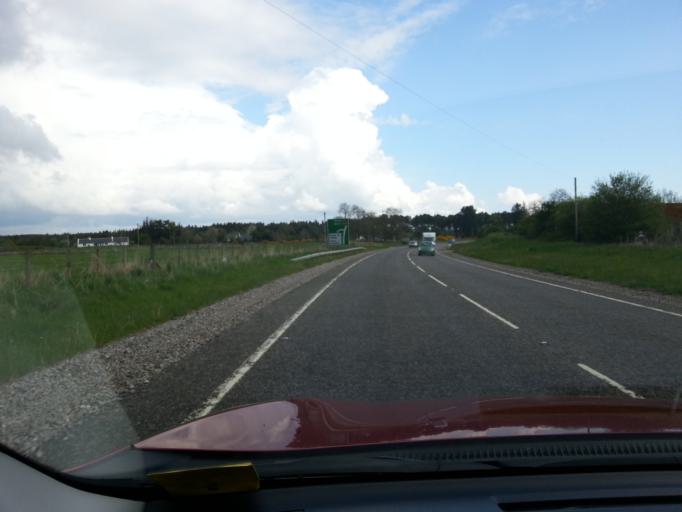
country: GB
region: Scotland
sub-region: Highland
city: Dornoch
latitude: 57.8751
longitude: -4.1100
